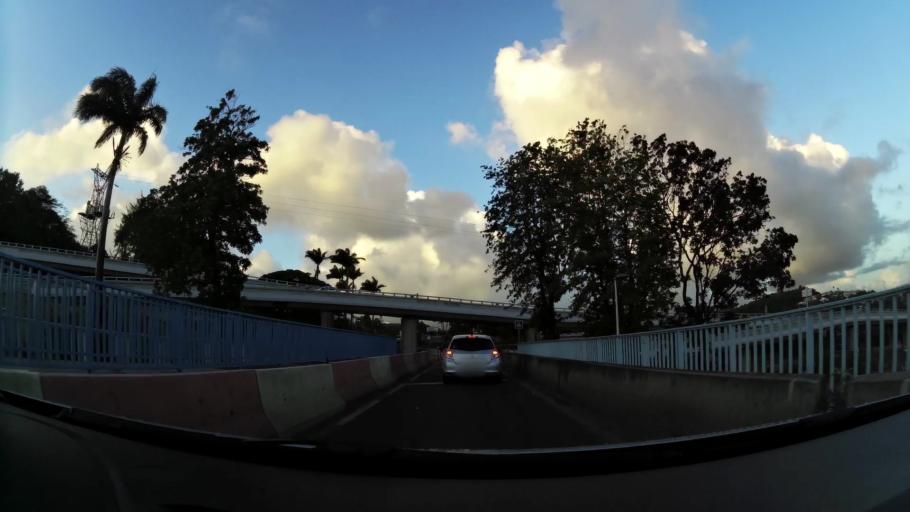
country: MQ
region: Martinique
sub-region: Martinique
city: Le Lamentin
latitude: 14.6182
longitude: -61.0390
